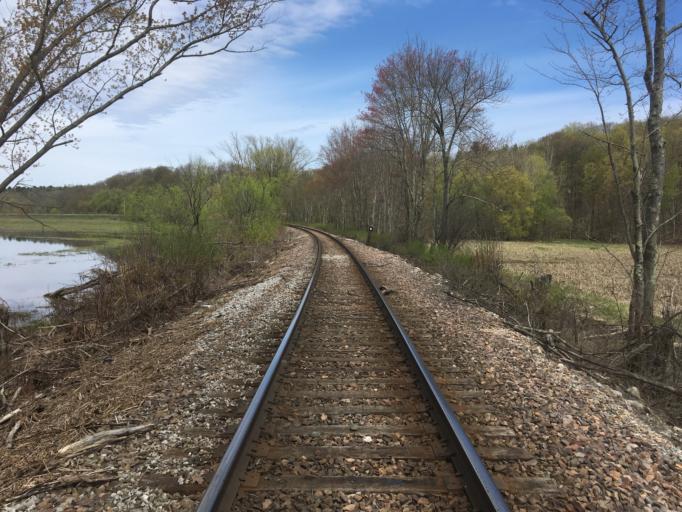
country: US
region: Vermont
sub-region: Rutland County
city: Brandon
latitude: 43.7078
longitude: -73.0363
